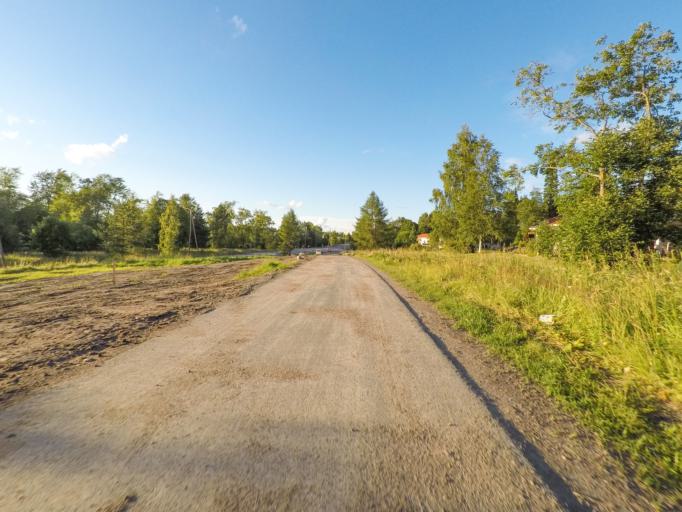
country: FI
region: South Karelia
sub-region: Imatra
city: Imatra
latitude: 61.2004
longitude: 28.7850
